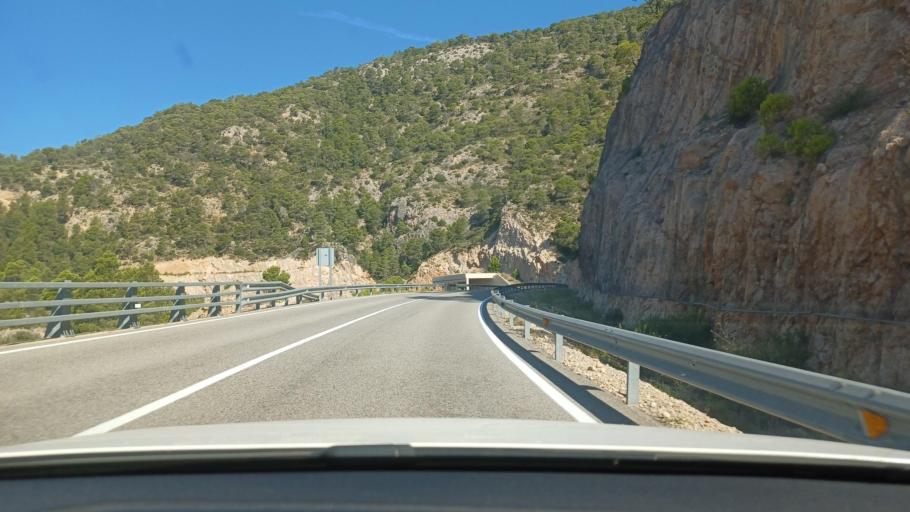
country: ES
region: Catalonia
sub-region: Provincia de Tarragona
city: Bot
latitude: 40.9712
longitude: 0.4357
